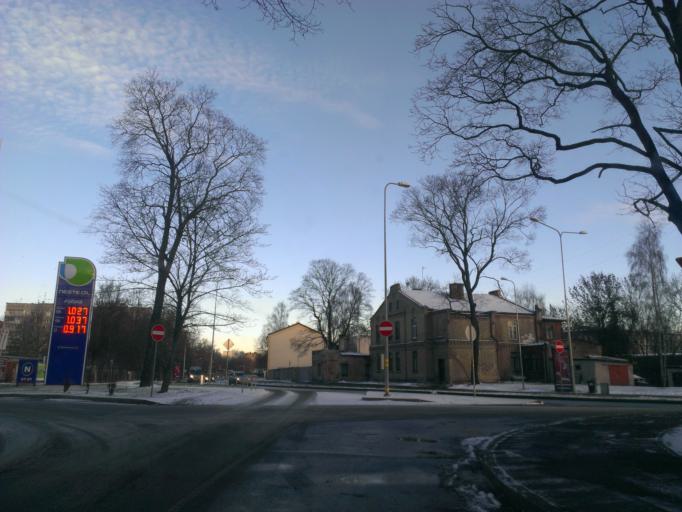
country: LV
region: Riga
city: Riga
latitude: 56.9533
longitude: 24.0696
